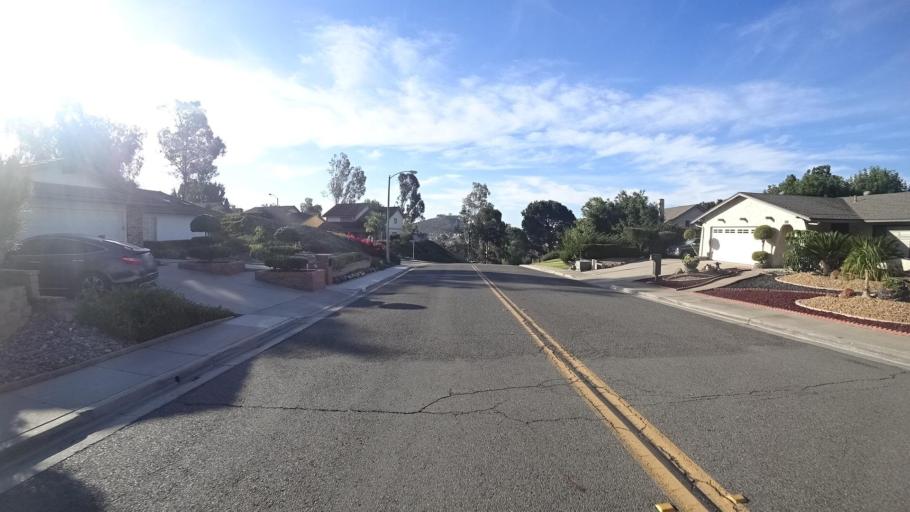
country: US
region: California
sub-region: San Diego County
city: Spring Valley
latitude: 32.7371
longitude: -116.9790
